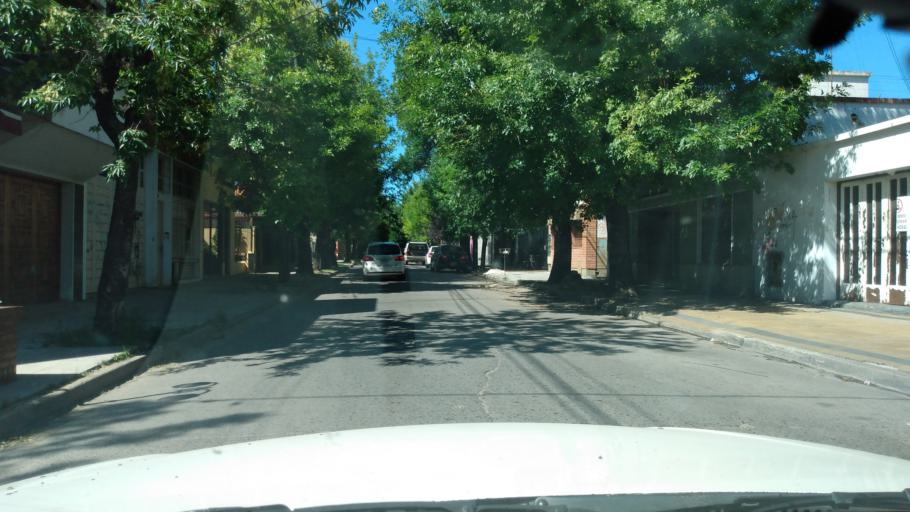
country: AR
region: Buenos Aires
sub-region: Partido de Lujan
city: Lujan
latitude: -34.5651
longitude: -59.1083
